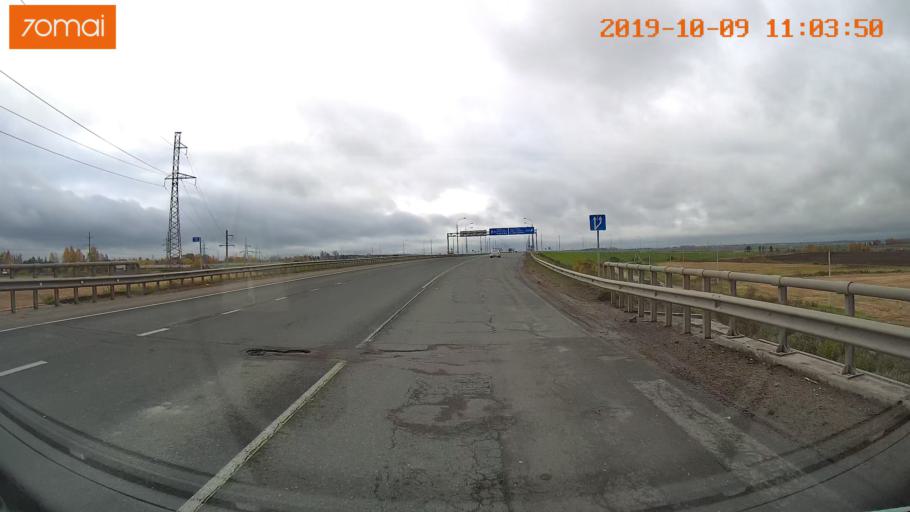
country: RU
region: Vologda
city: Vologda
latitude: 59.2183
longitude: 39.7737
